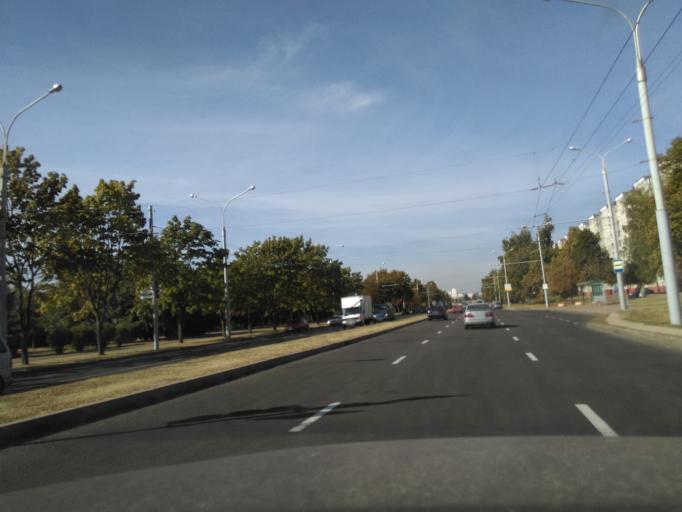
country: BY
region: Minsk
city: Minsk
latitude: 53.8522
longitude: 27.6135
